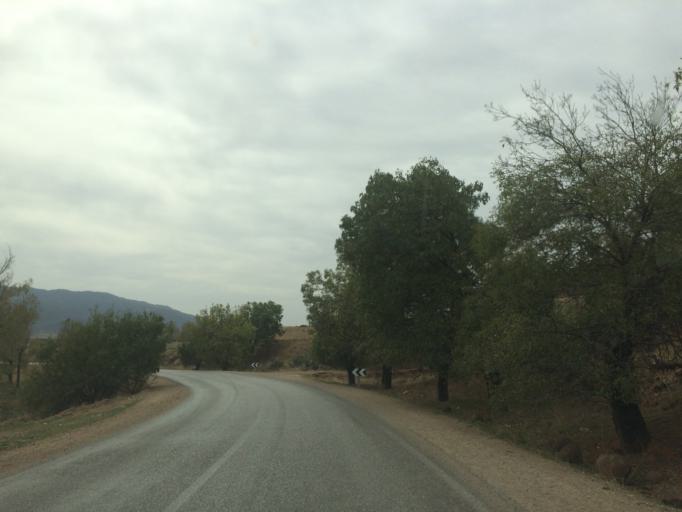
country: MA
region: Meknes-Tafilalet
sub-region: Ifrane
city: Azrou
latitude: 33.4677
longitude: -5.2434
